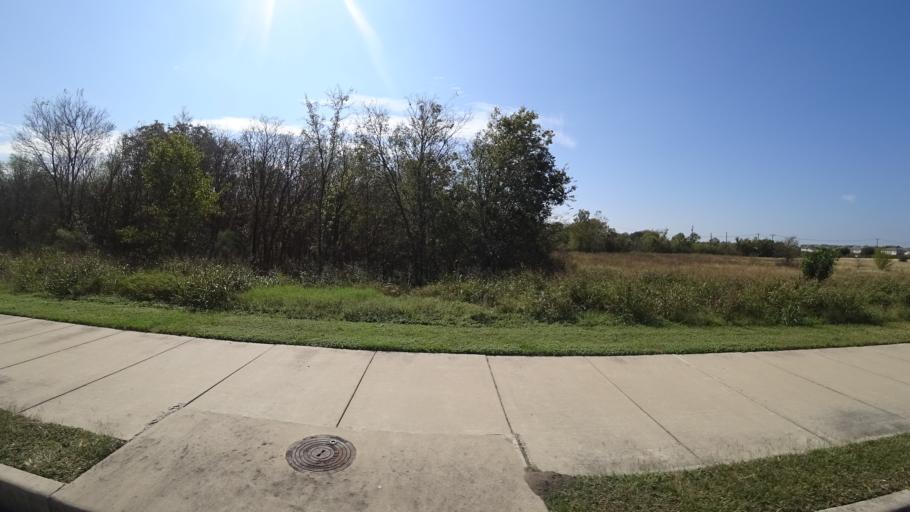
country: US
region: Texas
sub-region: Travis County
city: Pflugerville
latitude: 30.4272
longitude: -97.6315
